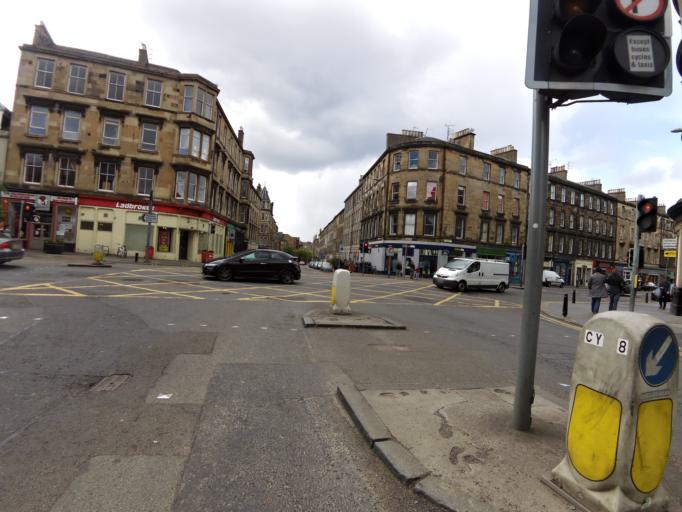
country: GB
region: Scotland
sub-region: Edinburgh
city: Edinburgh
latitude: 55.9391
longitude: -3.1792
